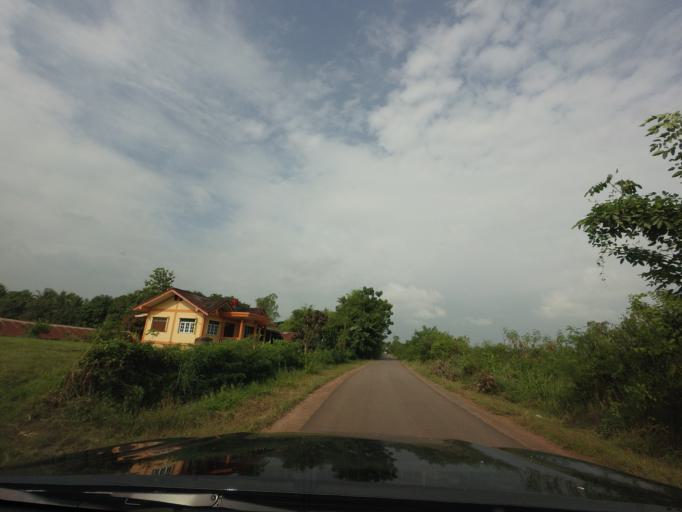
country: TH
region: Nong Khai
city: Nong Khai
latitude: 17.8129
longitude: 102.7304
